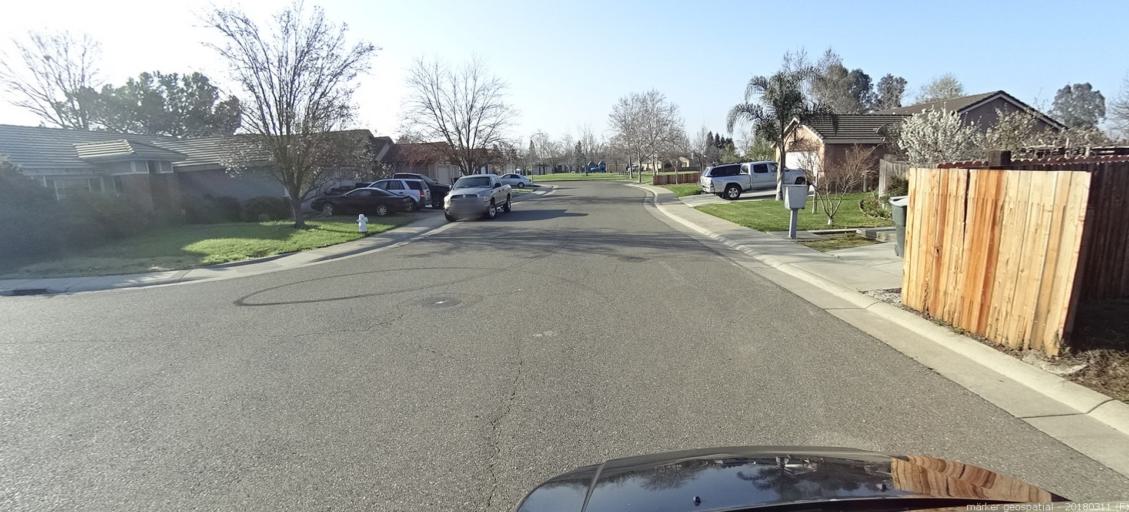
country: US
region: California
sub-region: Sacramento County
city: Vineyard
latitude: 38.4569
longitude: -121.3881
